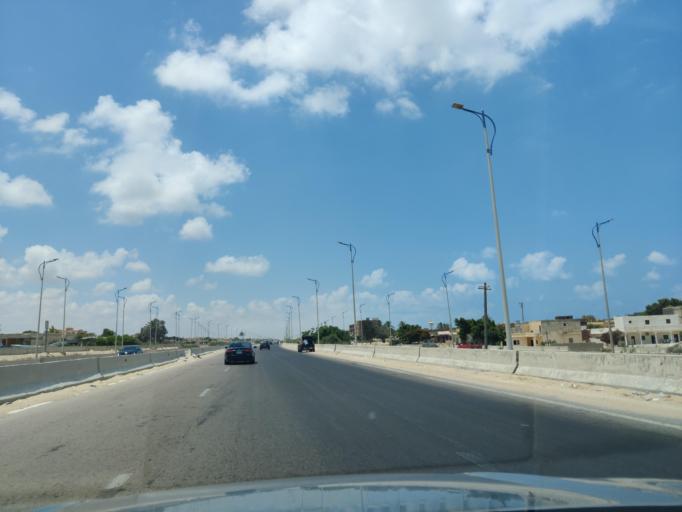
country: EG
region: Alexandria
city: Alexandria
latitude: 31.0020
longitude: 29.6137
